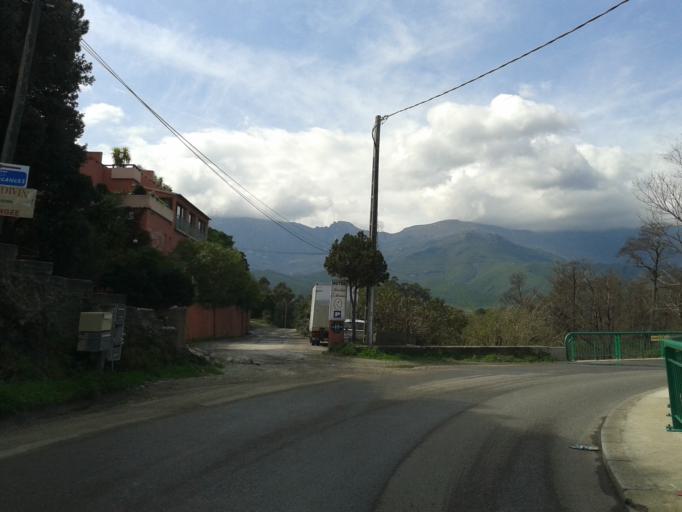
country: FR
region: Corsica
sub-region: Departement de la Haute-Corse
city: Brando
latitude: 42.8356
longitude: 9.4803
